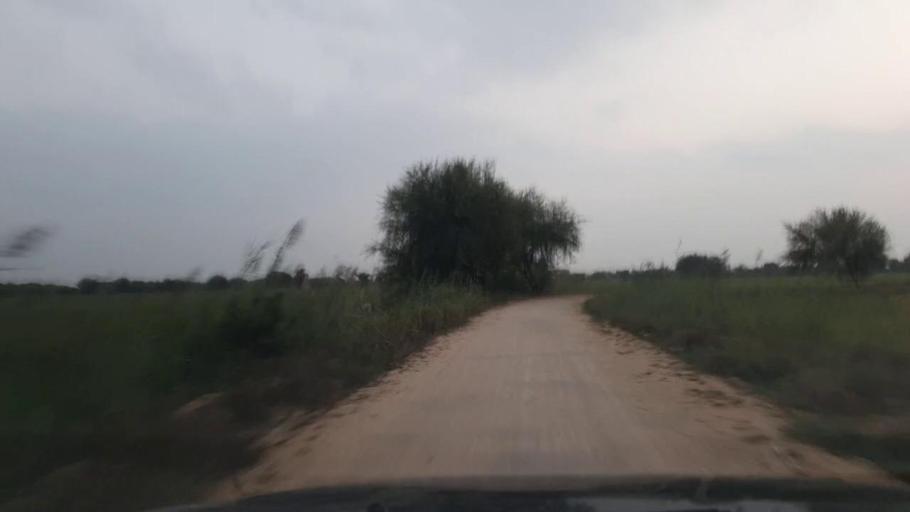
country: PK
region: Sindh
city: Jati
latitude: 24.5200
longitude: 68.3693
